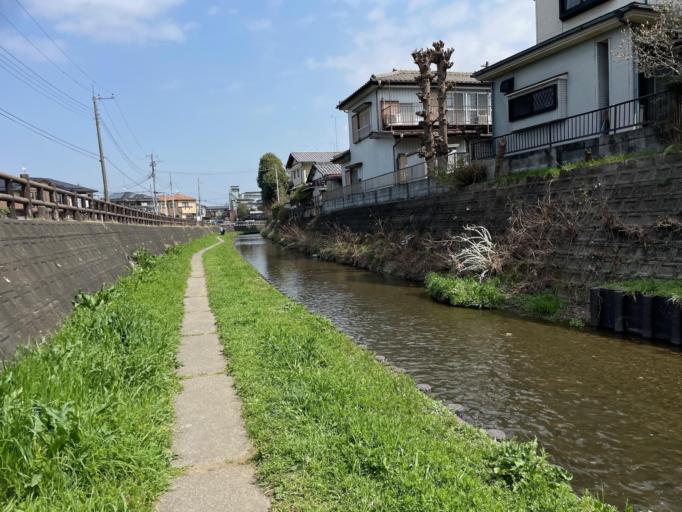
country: JP
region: Saitama
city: Kawagoe
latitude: 35.9276
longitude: 139.4807
